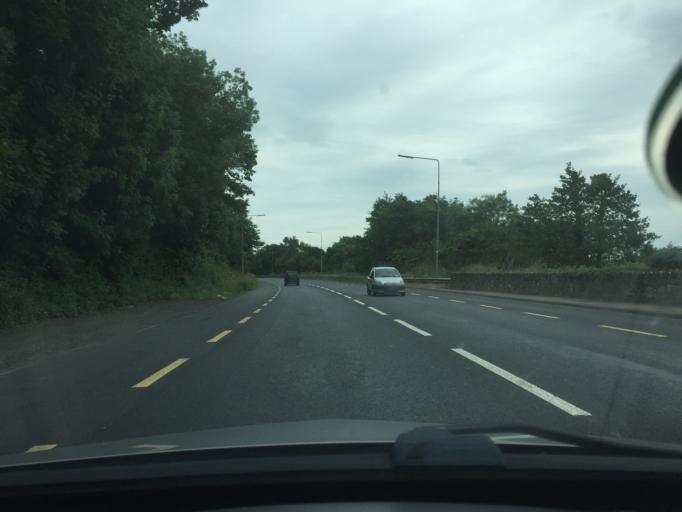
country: IE
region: Leinster
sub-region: Loch Garman
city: Enniscorthy
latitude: 52.4965
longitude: -6.5656
